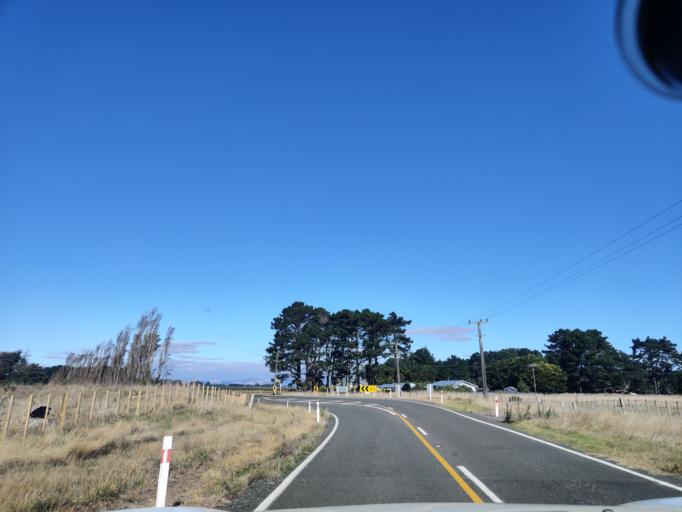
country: NZ
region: Manawatu-Wanganui
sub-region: Horowhenua District
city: Foxton
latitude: -40.3856
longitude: 175.2784
